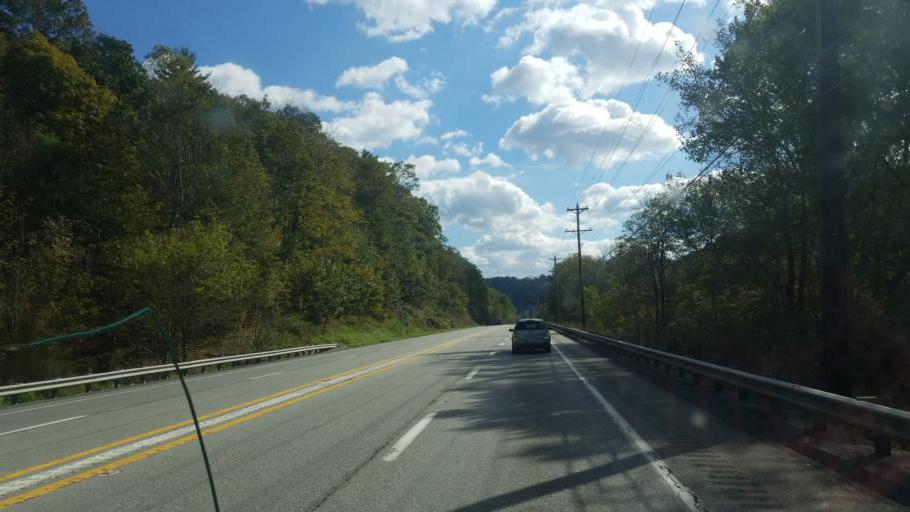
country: US
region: Pennsylvania
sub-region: Bedford County
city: Earlston
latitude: 39.9964
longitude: -78.2868
